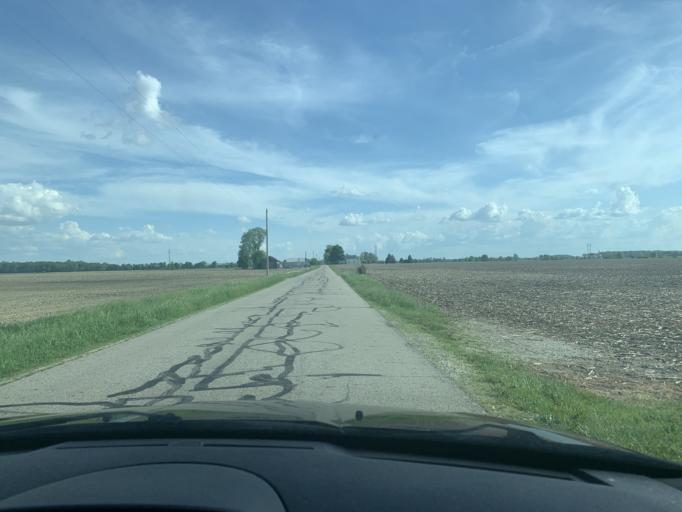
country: US
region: Ohio
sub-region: Logan County
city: De Graff
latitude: 40.2709
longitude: -84.0153
